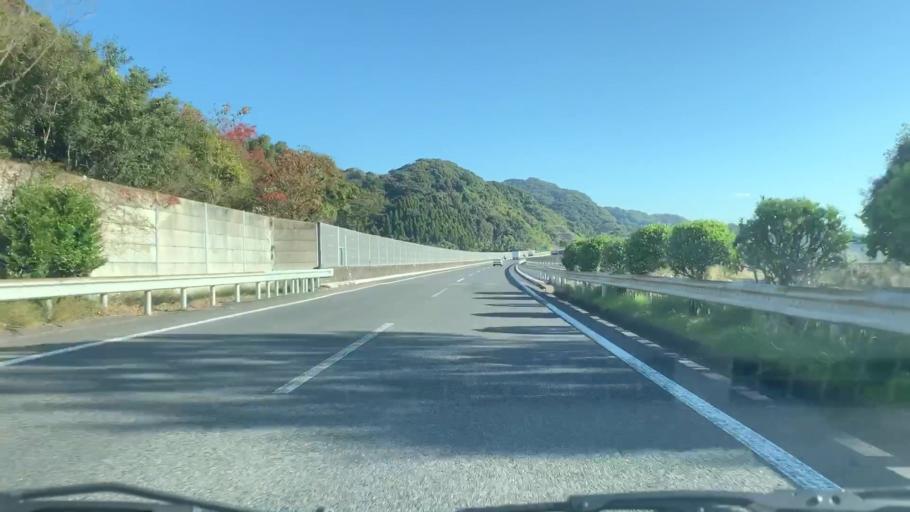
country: JP
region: Saga Prefecture
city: Saga-shi
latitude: 33.2952
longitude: 130.1713
